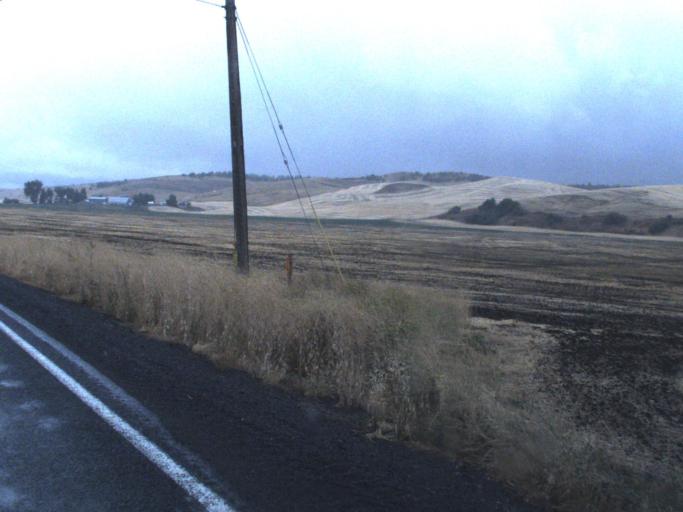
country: US
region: Washington
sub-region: Whitman County
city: Colfax
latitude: 47.0725
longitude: -117.5354
